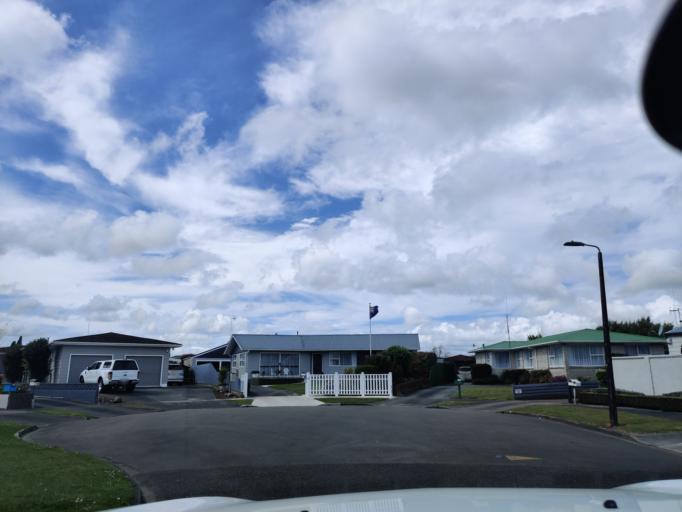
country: NZ
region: Manawatu-Wanganui
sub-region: Palmerston North City
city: Palmerston North
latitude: -40.3620
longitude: 175.5814
